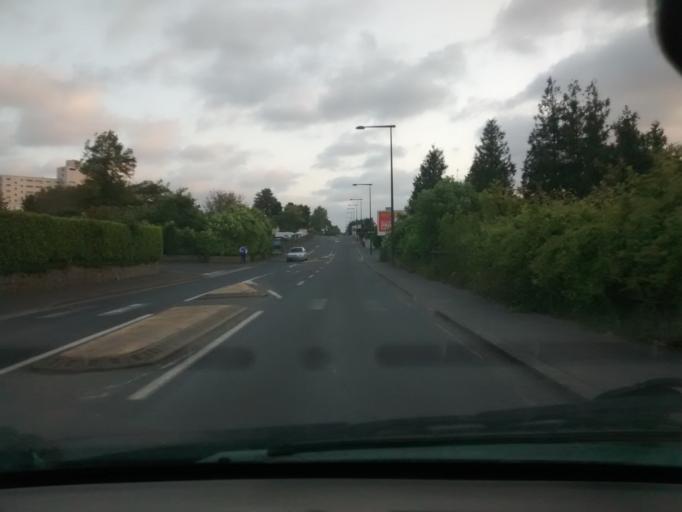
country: FR
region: Lower Normandy
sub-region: Departement de la Manche
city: Agneaux
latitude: 49.1090
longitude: -1.1056
